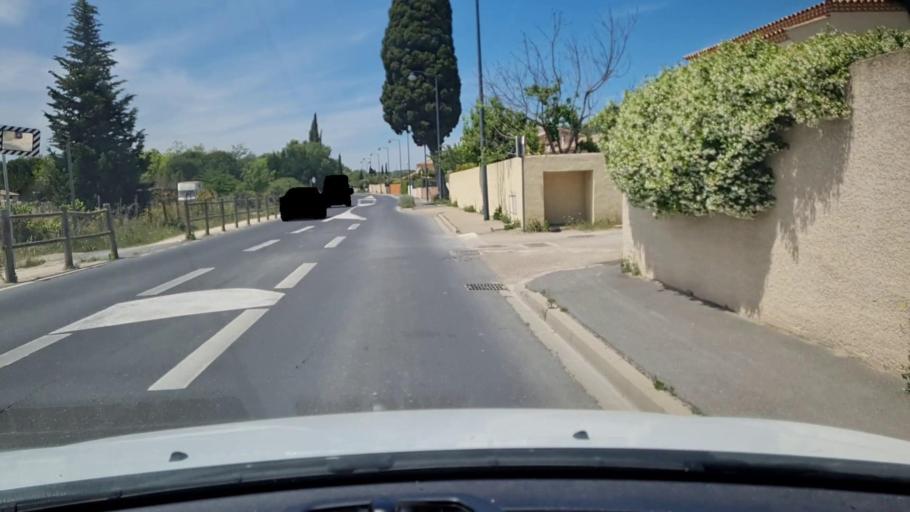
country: FR
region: Languedoc-Roussillon
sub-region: Departement du Gard
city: Aigues-Mortes
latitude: 43.5716
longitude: 4.1778
